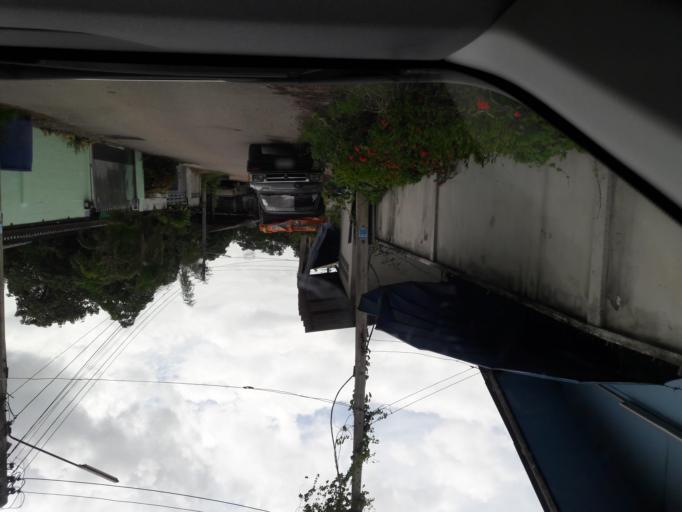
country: TH
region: Ratchaburi
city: Ratchaburi
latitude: 13.5348
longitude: 99.7944
